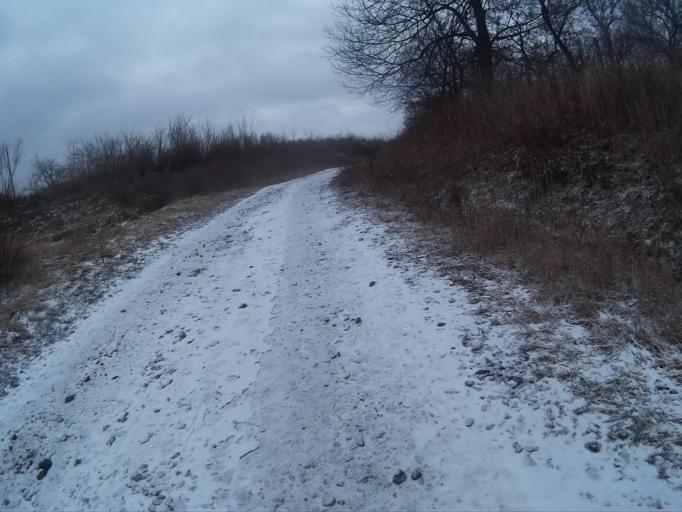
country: HU
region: Borsod-Abauj-Zemplen
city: Halmaj
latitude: 48.3698
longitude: 20.9220
